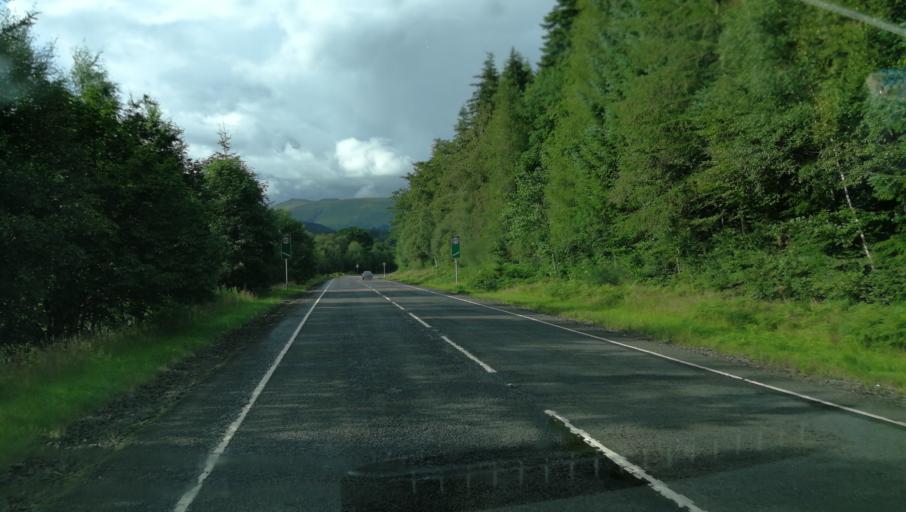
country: GB
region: Scotland
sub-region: Stirling
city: Callander
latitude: 56.3146
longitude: -4.3289
